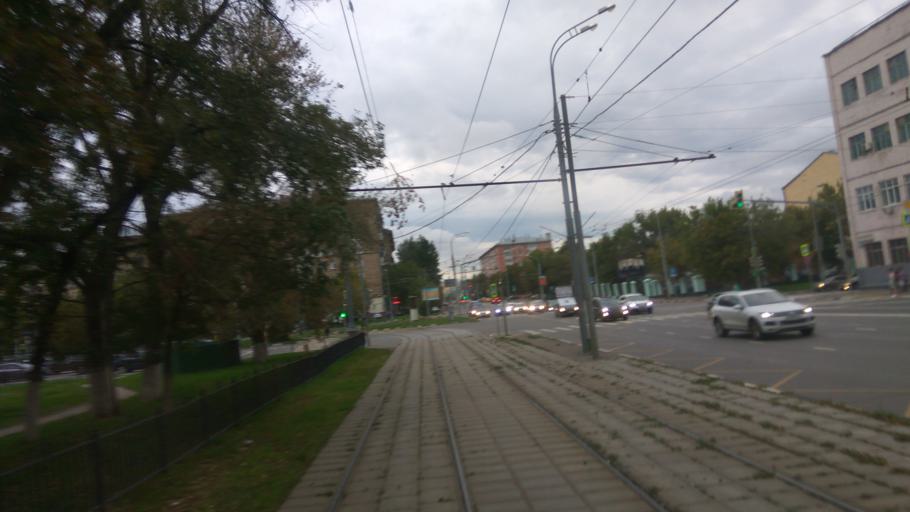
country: RU
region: Moscow
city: Taganskiy
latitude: 55.7203
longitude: 37.6746
